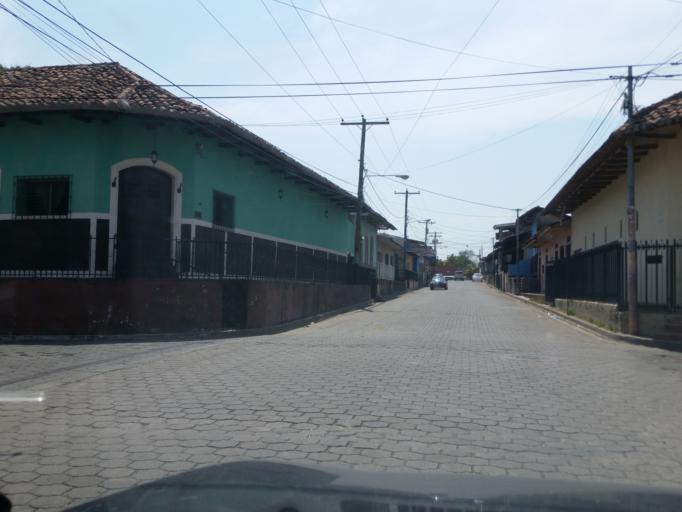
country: NI
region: Granada
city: Granada
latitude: 11.9259
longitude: -85.9603
